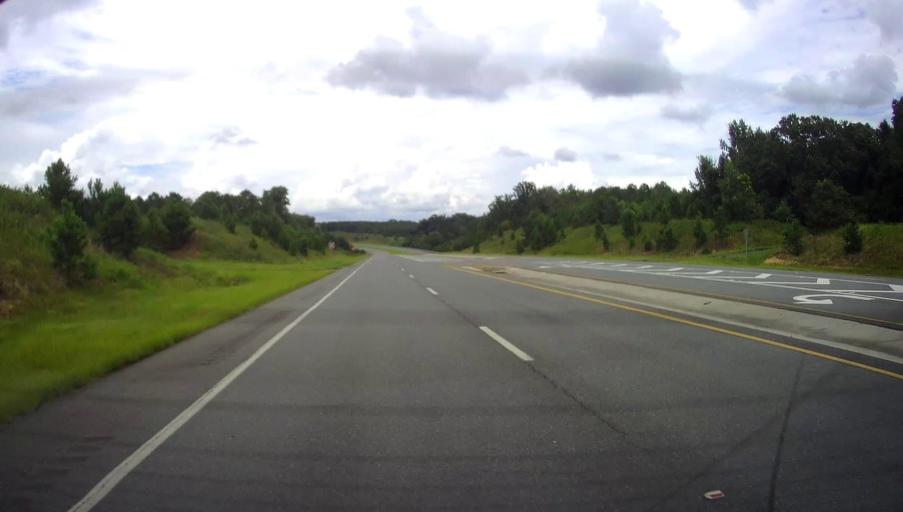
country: US
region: Georgia
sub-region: Schley County
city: Ellaville
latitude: 32.2446
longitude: -84.2966
